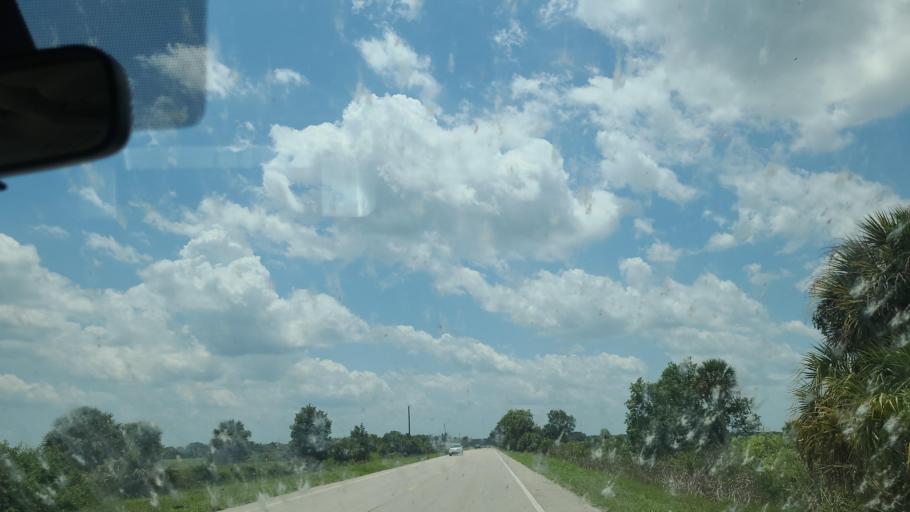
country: US
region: Florida
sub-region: Glades County
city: Buckhead Ridge
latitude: 27.1537
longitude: -81.0942
